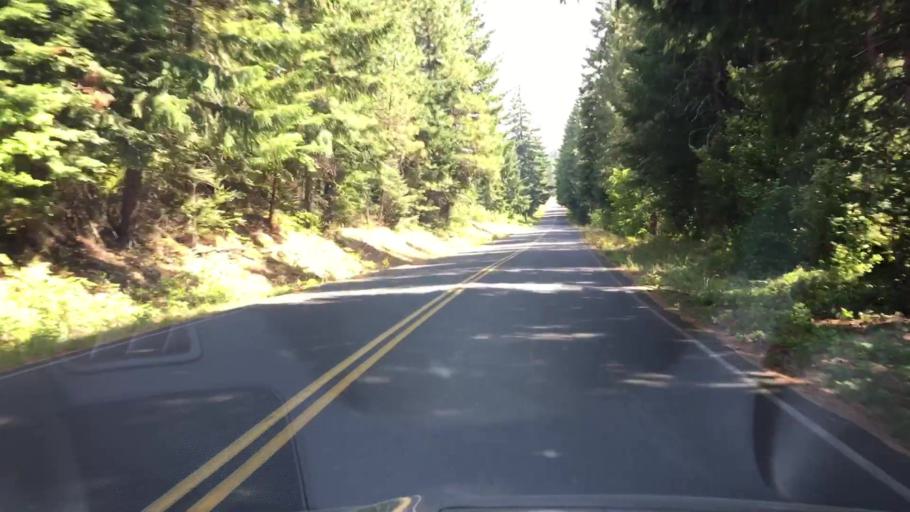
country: US
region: Washington
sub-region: Klickitat County
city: White Salmon
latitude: 46.0413
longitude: -121.5503
